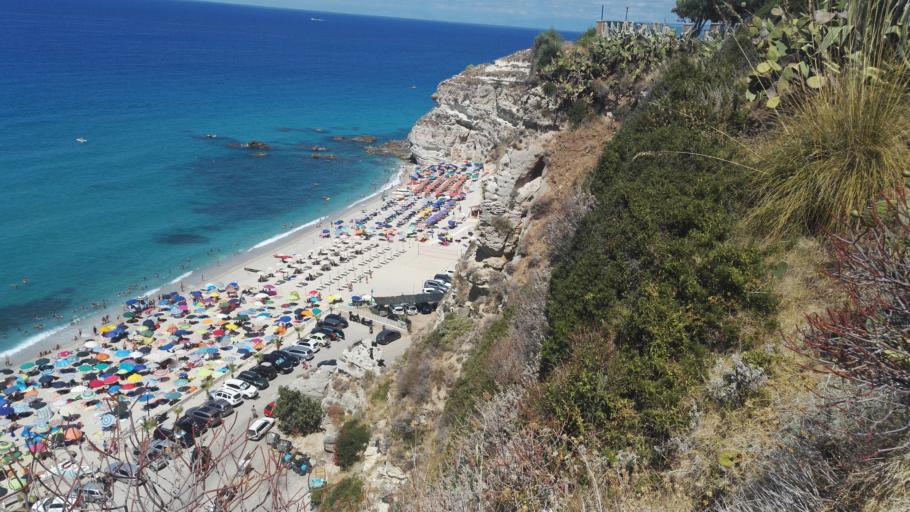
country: IT
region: Calabria
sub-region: Provincia di Vibo-Valentia
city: Santa Domenica
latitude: 38.6705
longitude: 15.8706
